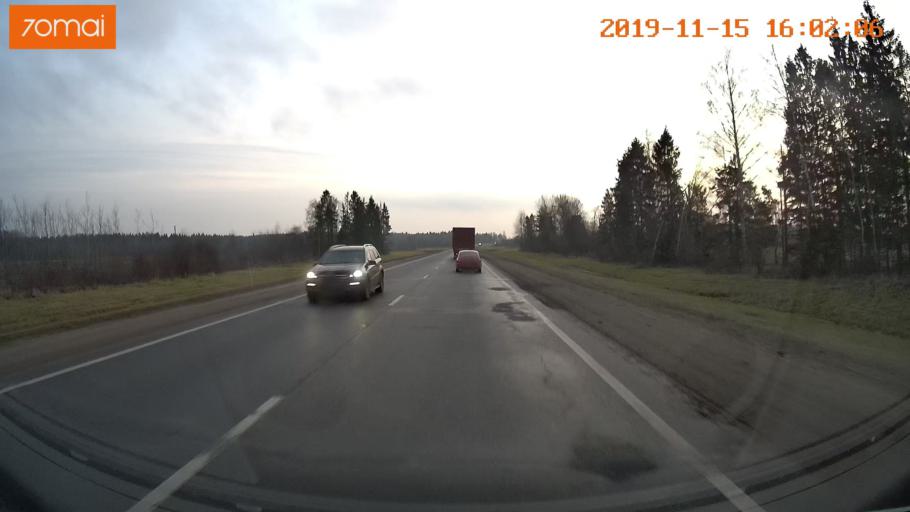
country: RU
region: Jaroslavl
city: Yaroslavl
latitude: 57.7752
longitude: 39.9269
